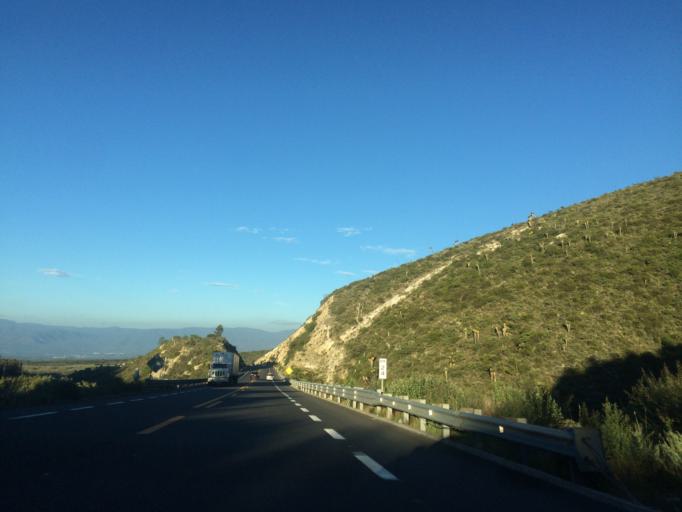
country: MX
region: Puebla
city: Chapuco
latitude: 18.6220
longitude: -97.4675
